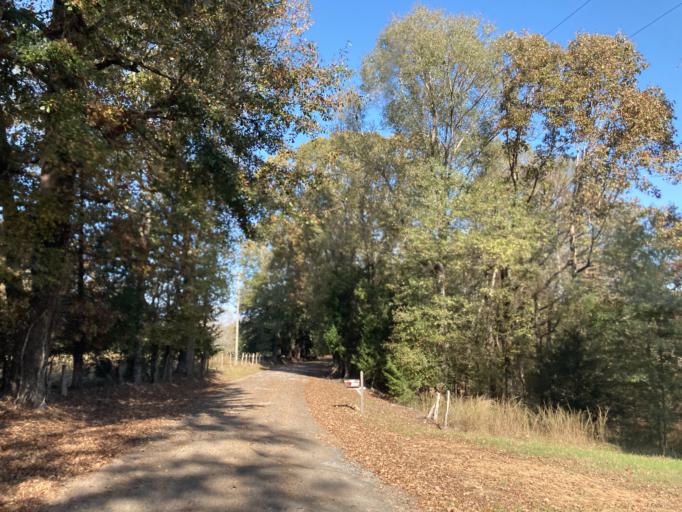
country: US
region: Mississippi
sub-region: Madison County
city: Kearney Park
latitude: 32.7354
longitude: -90.3179
